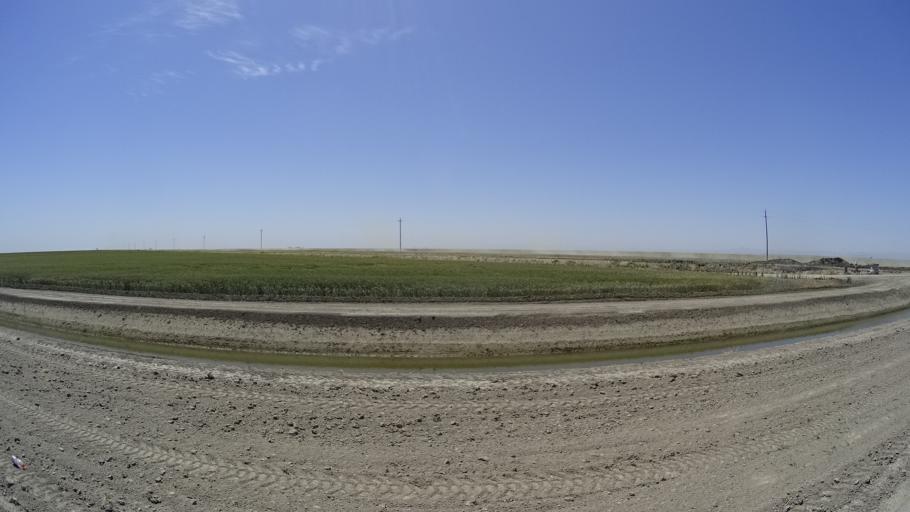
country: US
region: California
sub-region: Kings County
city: Corcoran
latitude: 36.1233
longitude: -119.6972
